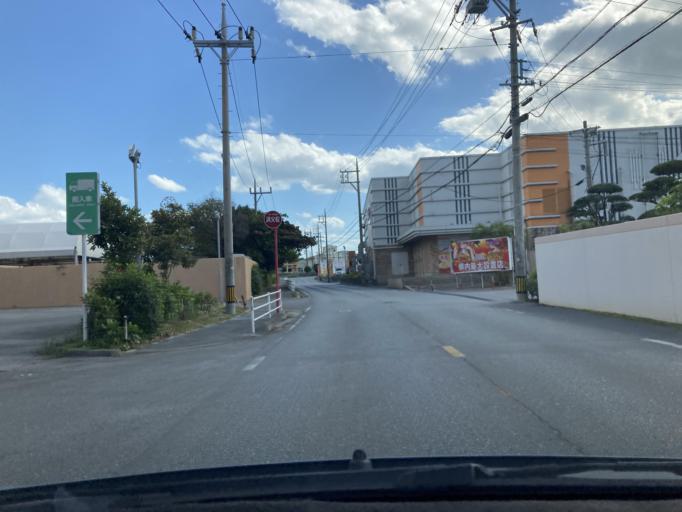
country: JP
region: Okinawa
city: Katsuren-haebaru
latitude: 26.3375
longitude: 127.8434
